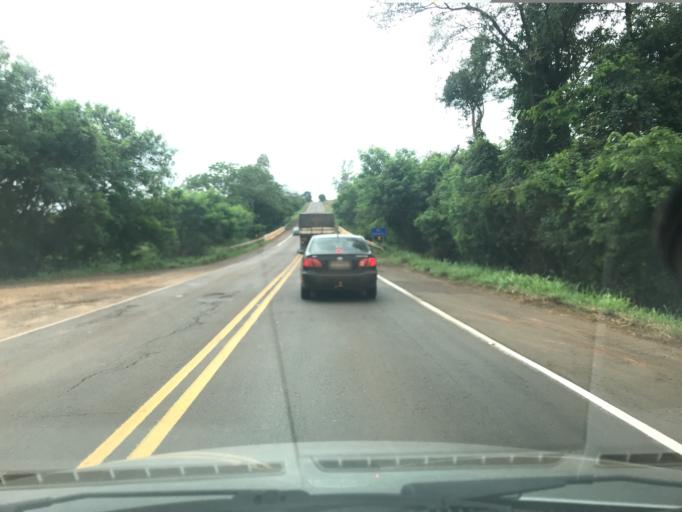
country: BR
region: Parana
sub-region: Terra Boa
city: Terra Boa
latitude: -23.6157
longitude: -52.4310
